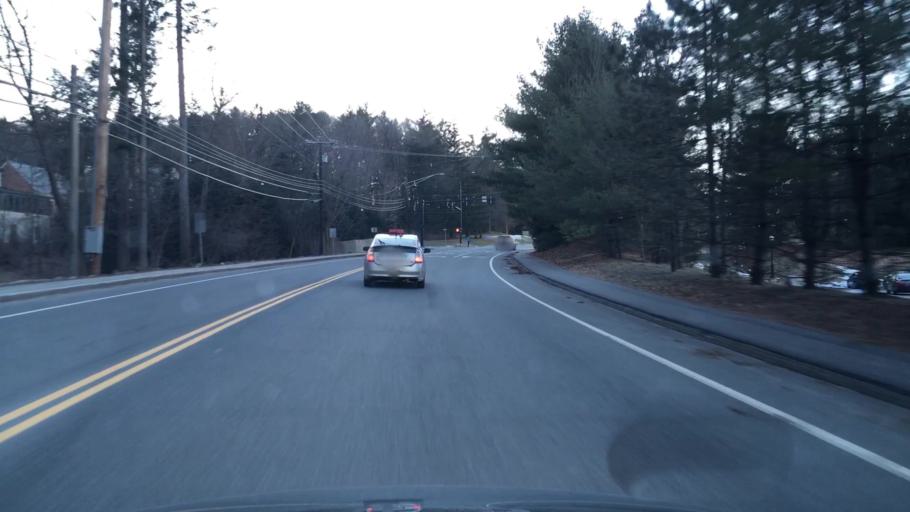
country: US
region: New Hampshire
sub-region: Grafton County
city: Hanover
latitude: 43.7084
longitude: -72.2818
